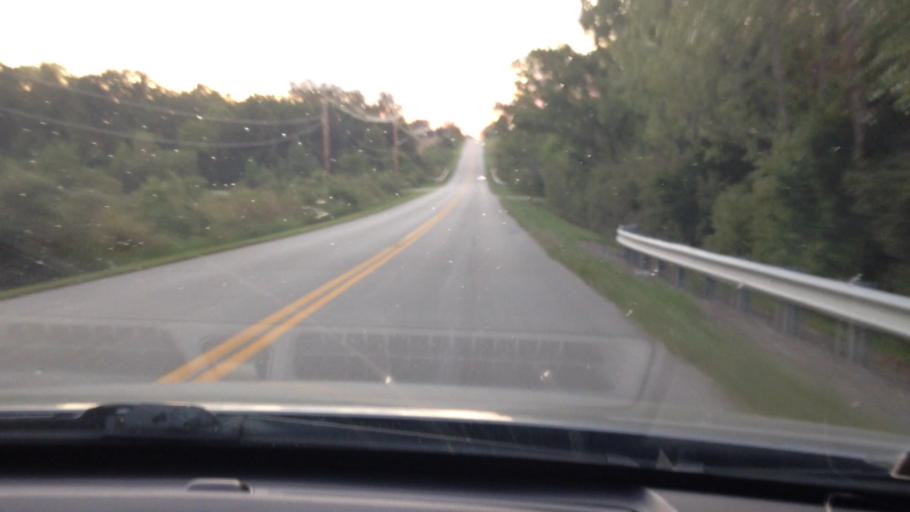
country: US
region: Kansas
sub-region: Leavenworth County
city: Lansing
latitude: 39.1867
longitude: -94.8525
